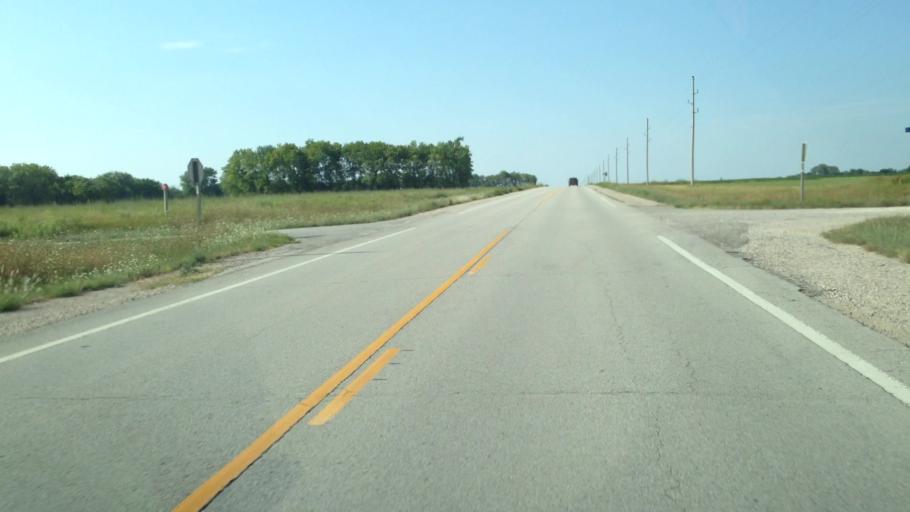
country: US
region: Kansas
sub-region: Anderson County
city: Garnett
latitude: 38.0412
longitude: -95.1697
